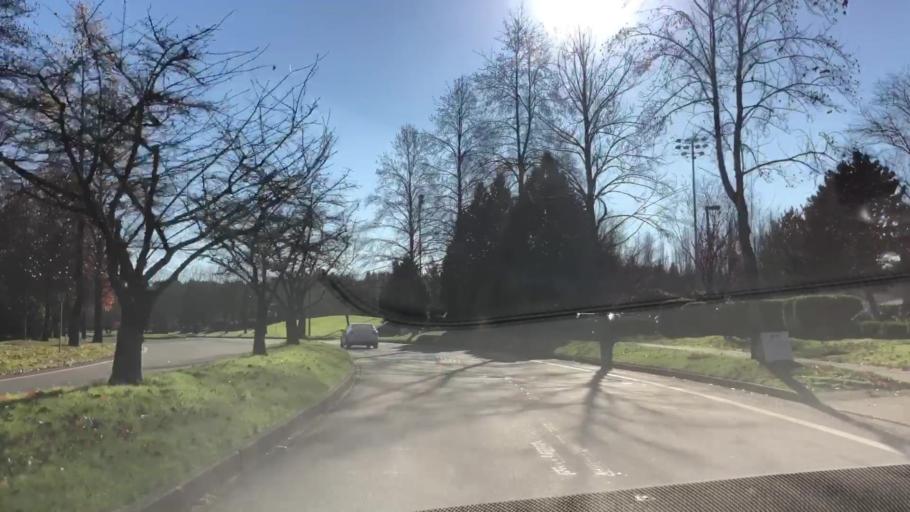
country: US
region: Washington
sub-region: King County
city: Woodinville
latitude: 47.7677
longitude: -122.1801
